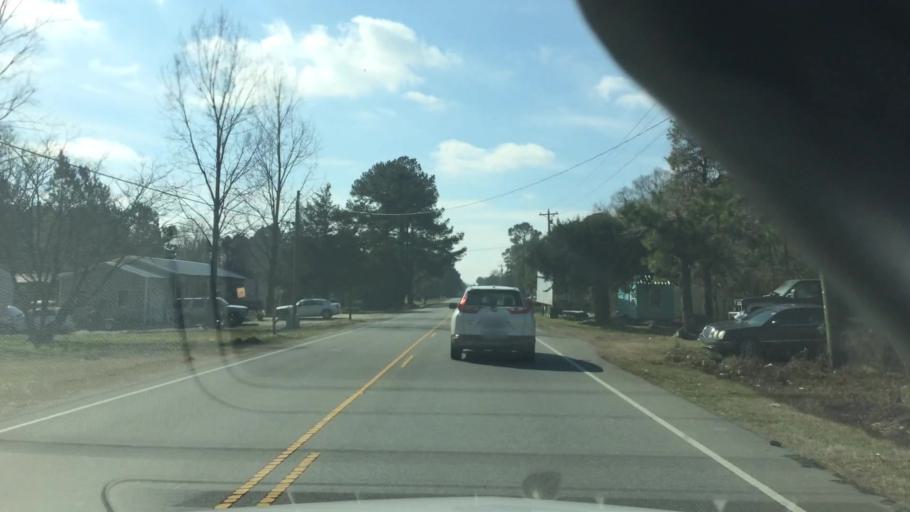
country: US
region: North Carolina
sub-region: Duplin County
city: Wallace
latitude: 34.7758
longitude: -77.9162
